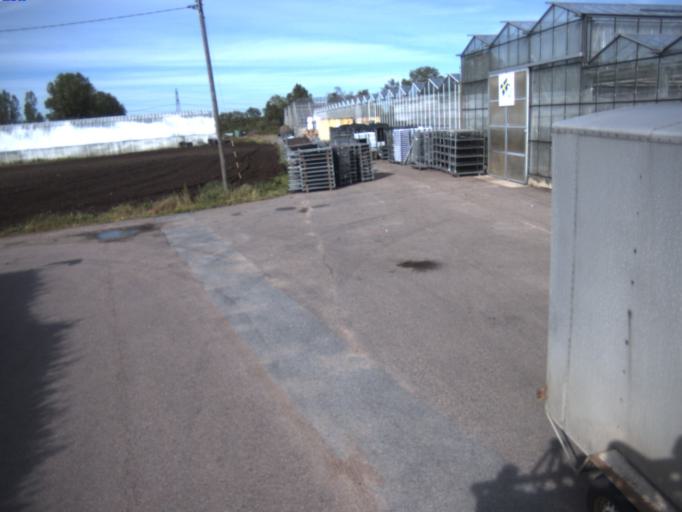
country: SE
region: Skane
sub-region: Helsingborg
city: Odakra
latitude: 56.0838
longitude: 12.7510
